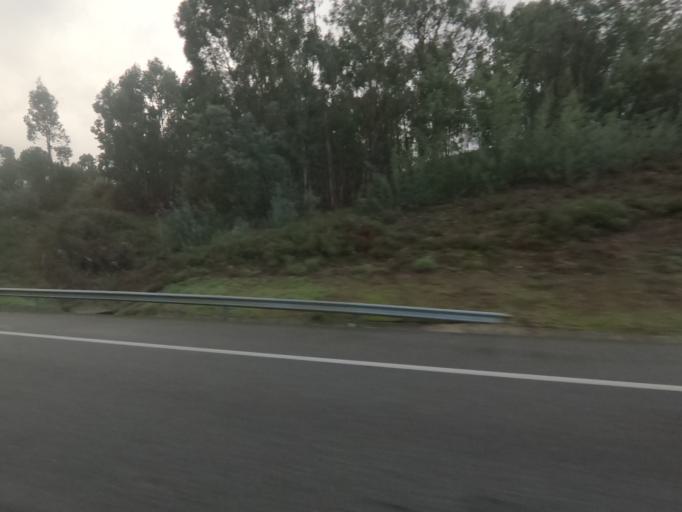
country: PT
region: Viana do Castelo
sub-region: Ponte de Lima
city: Ponte de Lima
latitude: 41.7810
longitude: -8.5690
